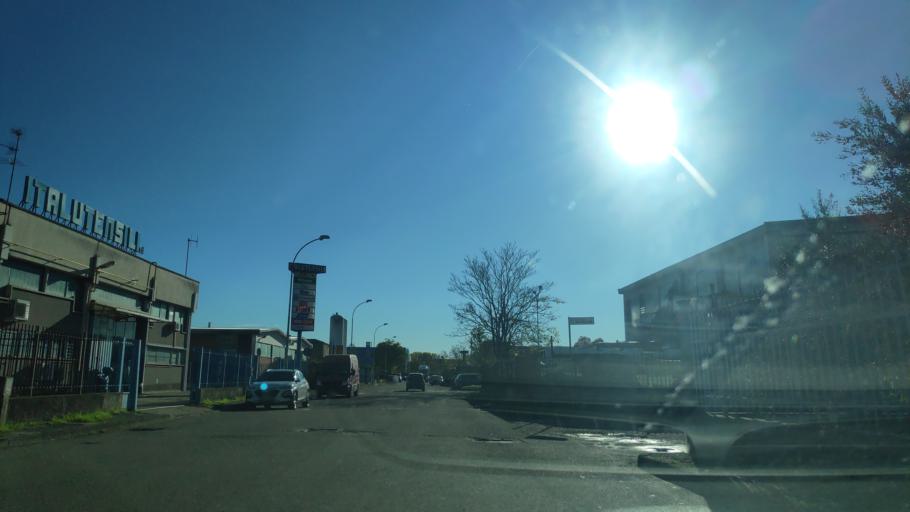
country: IT
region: Lombardy
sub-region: Citta metropolitana di Milano
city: Rozzano
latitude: 45.3751
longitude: 9.1739
